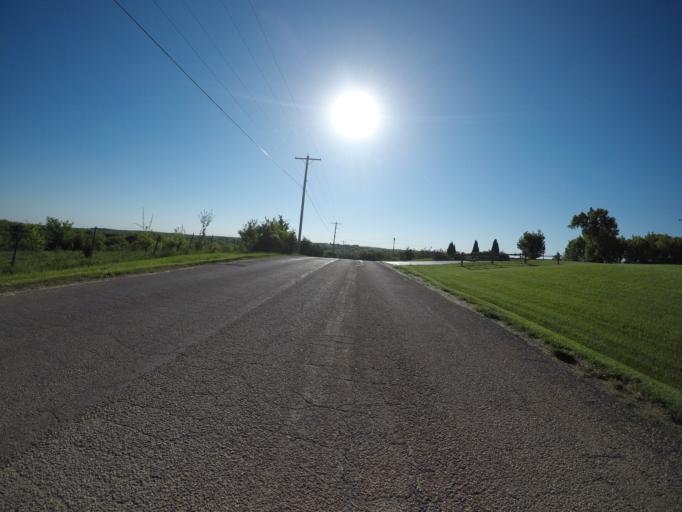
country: US
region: Kansas
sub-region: Shawnee County
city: Topeka
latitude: 39.0224
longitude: -95.5550
